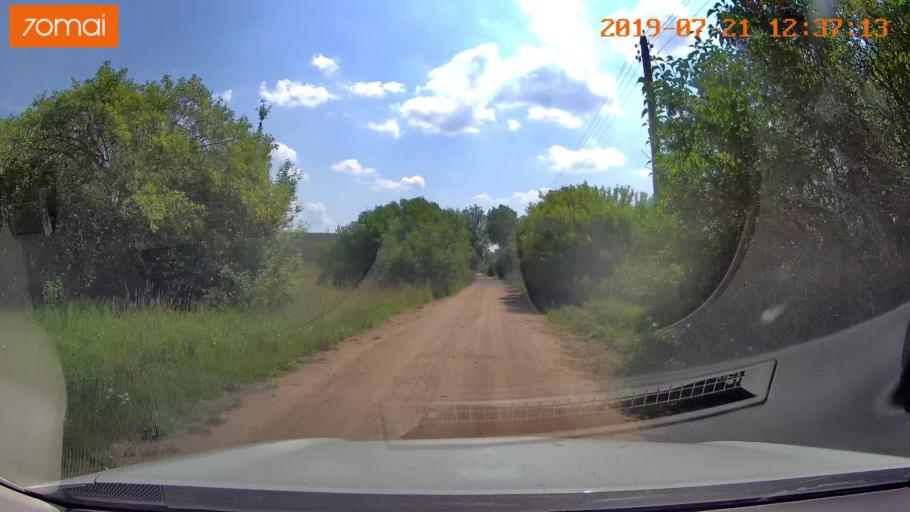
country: BY
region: Grodnenskaya
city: Lyubcha
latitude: 53.8653
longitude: 26.0041
